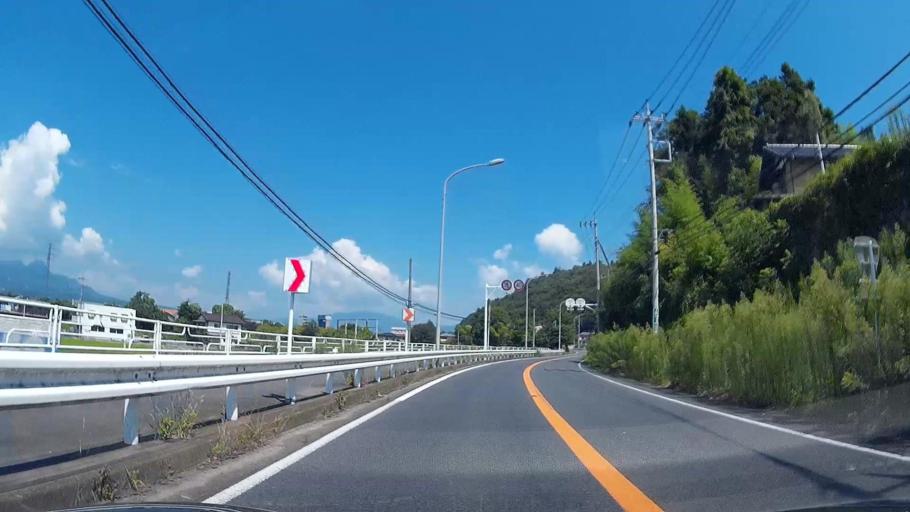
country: JP
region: Gunma
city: Shibukawa
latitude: 36.4488
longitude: 139.0459
